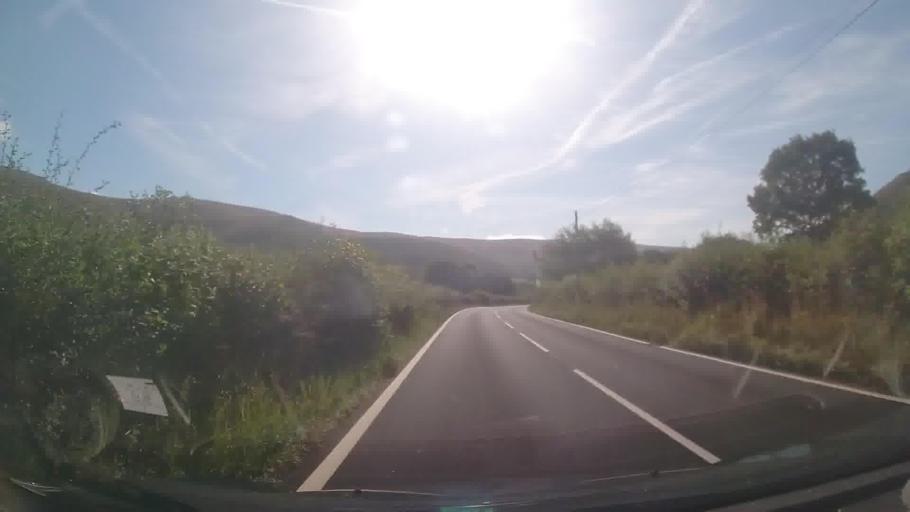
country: GB
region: Wales
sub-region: Sir Powys
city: Hay
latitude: 51.9514
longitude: -3.1946
